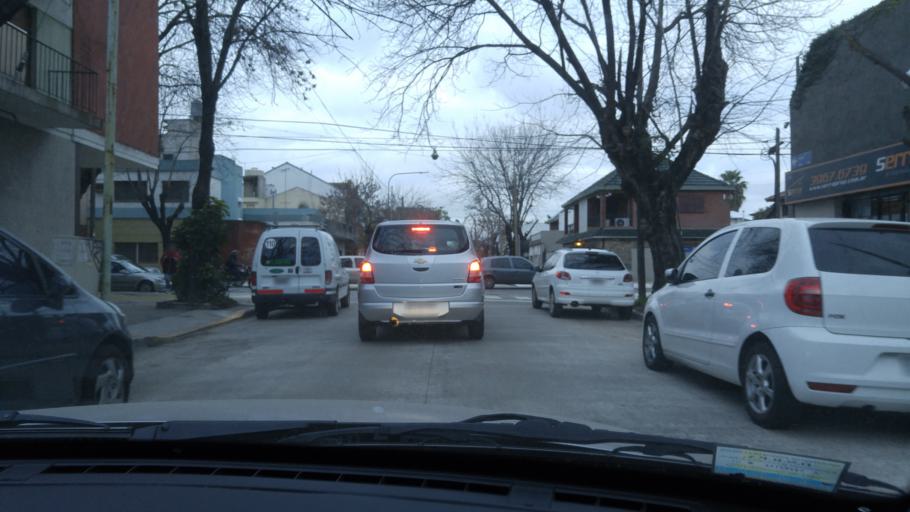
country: AR
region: Buenos Aires F.D.
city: Villa Santa Rita
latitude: -34.6172
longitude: -58.5233
